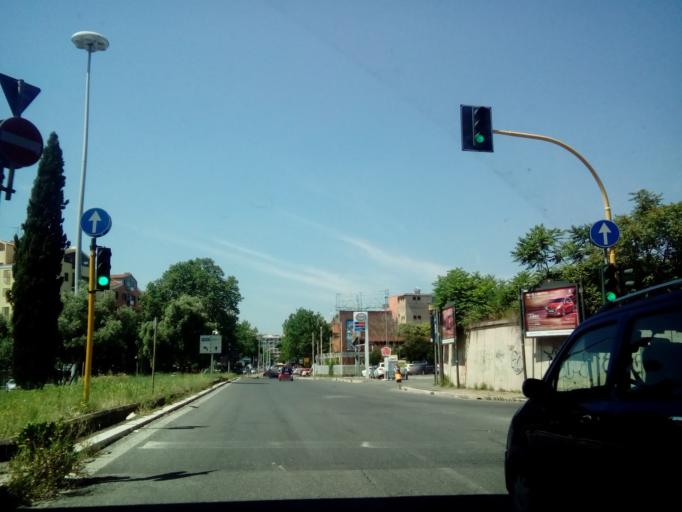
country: IT
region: Latium
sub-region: Citta metropolitana di Roma Capitale
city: Rome
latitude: 41.9124
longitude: 12.5536
